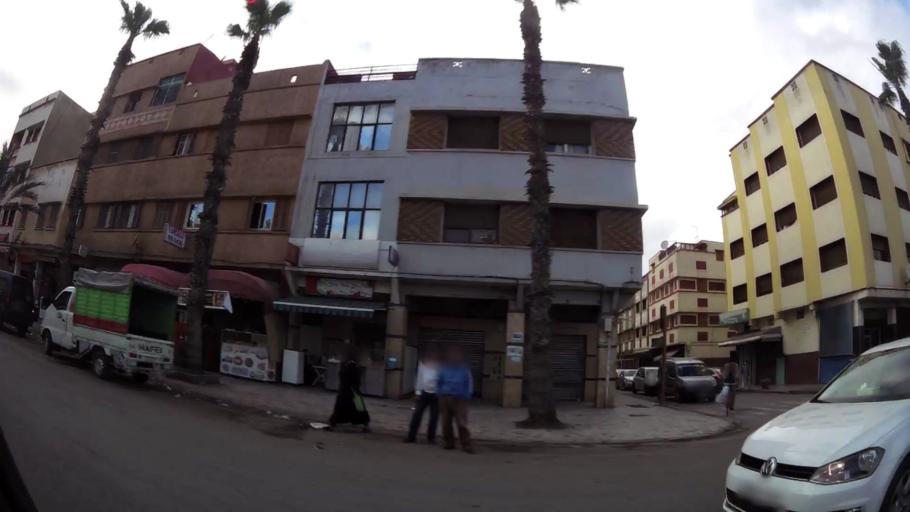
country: MA
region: Grand Casablanca
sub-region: Mohammedia
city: Mohammedia
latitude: 33.6870
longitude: -7.3810
